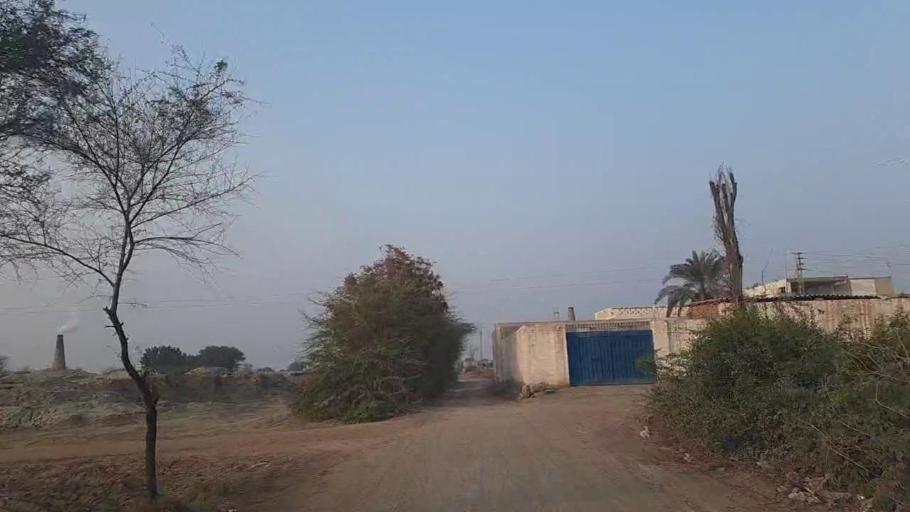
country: PK
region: Sindh
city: Nawabshah
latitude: 26.2809
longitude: 68.4648
